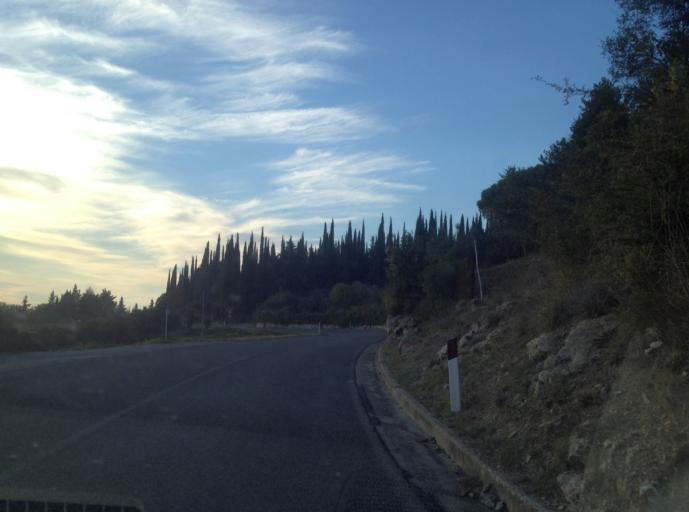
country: IT
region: Tuscany
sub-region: Provincia di Siena
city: Castellina in Chianti
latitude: 43.4397
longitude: 11.3047
